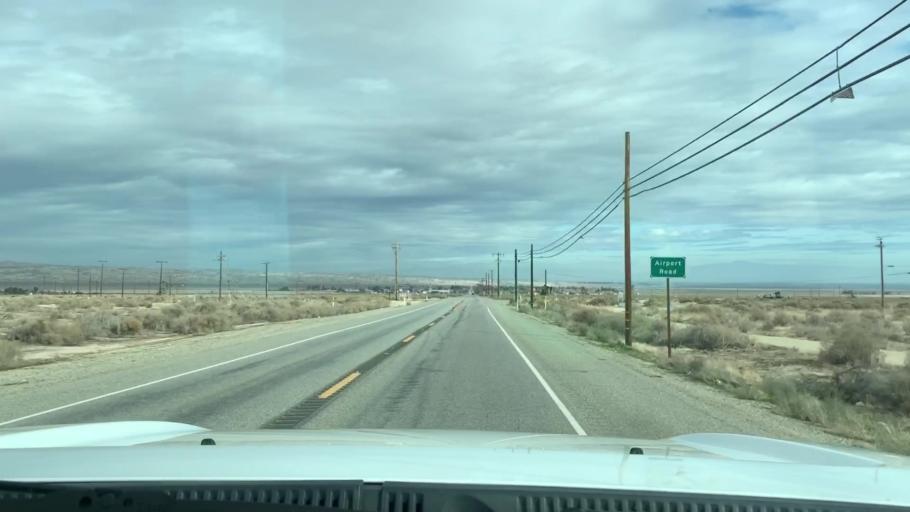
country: US
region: California
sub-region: Kern County
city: Ford City
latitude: 35.1927
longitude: -119.4304
